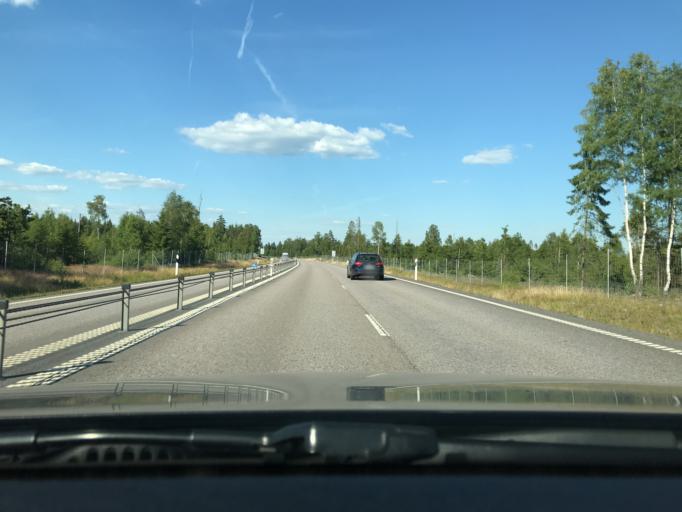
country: SE
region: Kronoberg
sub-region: Alvesta Kommun
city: Vislanda
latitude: 56.6630
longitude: 14.2989
